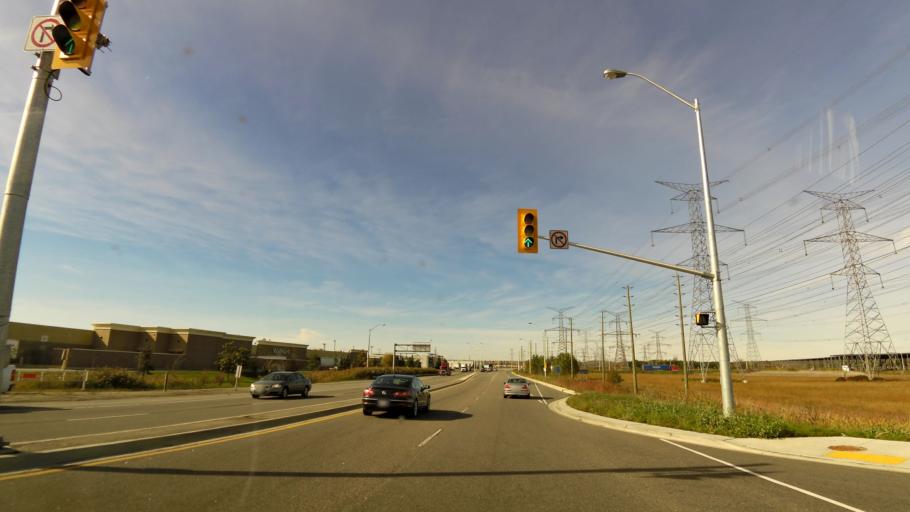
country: CA
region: Ontario
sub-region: Halton
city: Milton
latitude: 43.5429
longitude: -79.8648
